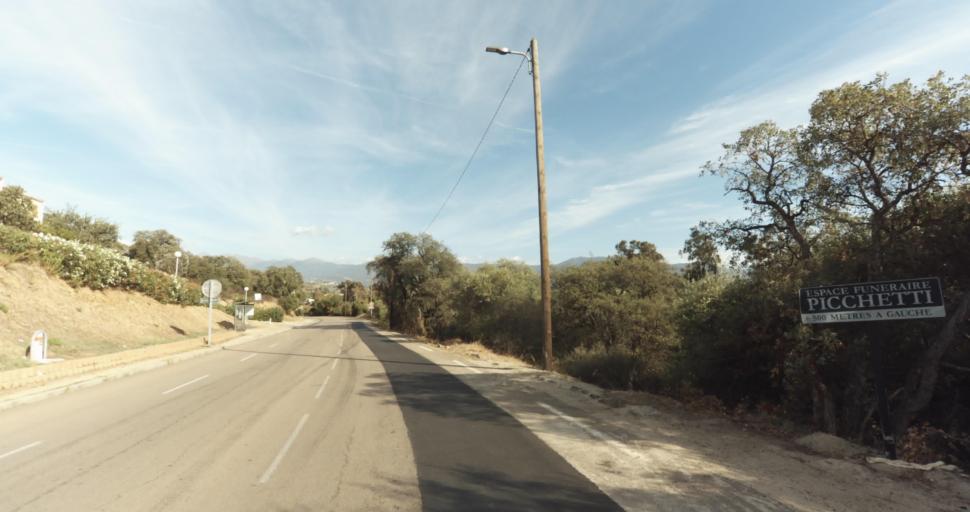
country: FR
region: Corsica
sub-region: Departement de la Corse-du-Sud
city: Ajaccio
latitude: 41.9300
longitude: 8.7806
